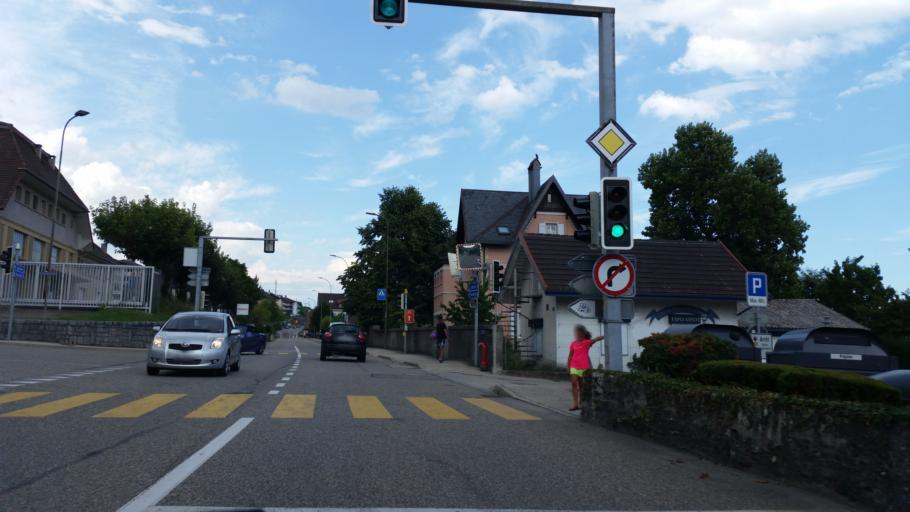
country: CH
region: Neuchatel
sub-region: Boudry District
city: Gorgier
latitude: 46.8990
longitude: 6.7838
